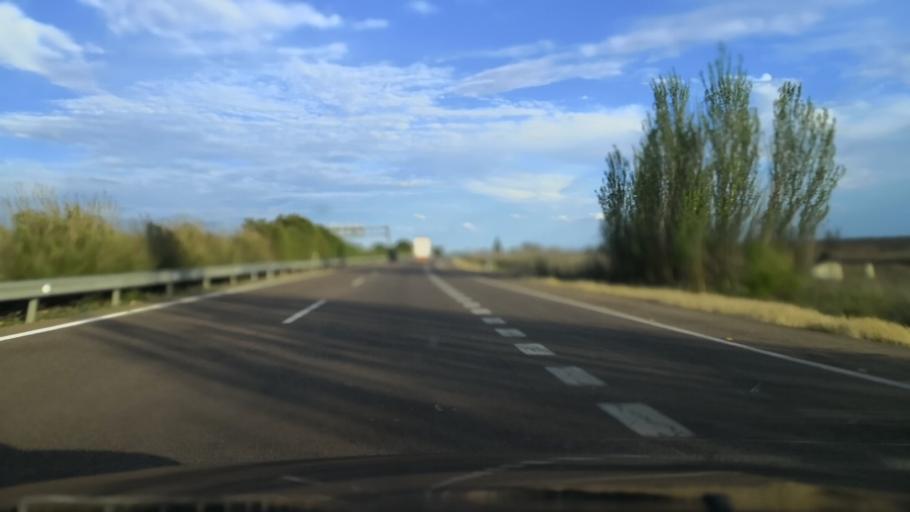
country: ES
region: Extremadura
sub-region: Provincia de Badajoz
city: Talavera La Real
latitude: 38.8635
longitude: -6.7530
